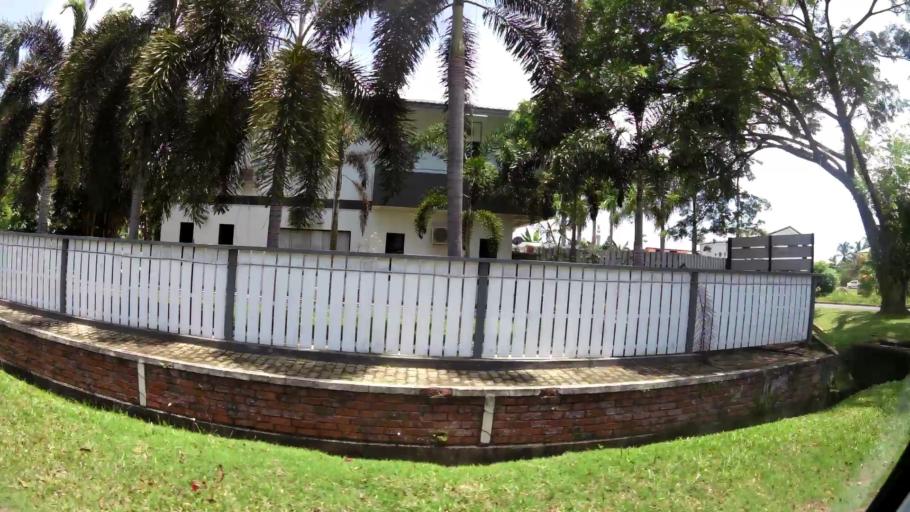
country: BN
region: Belait
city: Kuala Belait
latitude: 4.5853
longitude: 114.2370
